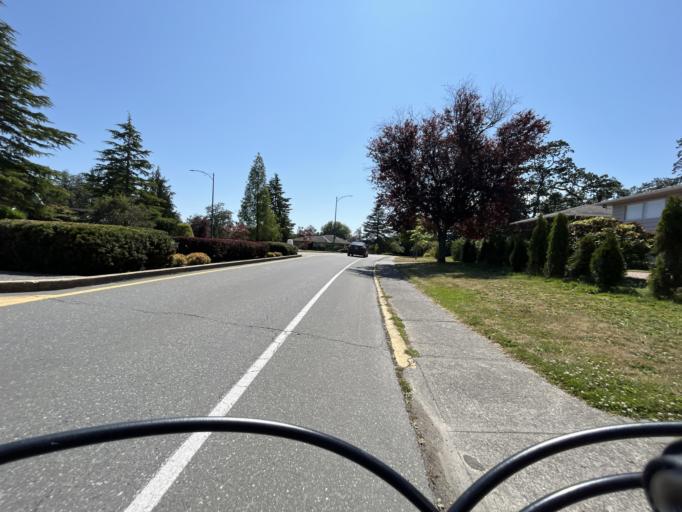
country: CA
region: British Columbia
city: Oak Bay
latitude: 48.4503
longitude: -123.3168
